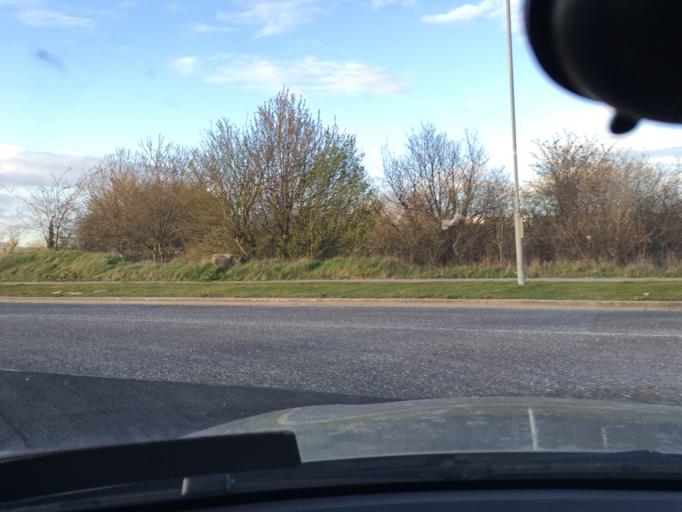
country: IE
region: Leinster
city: Hartstown
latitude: 53.4071
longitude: -6.4106
